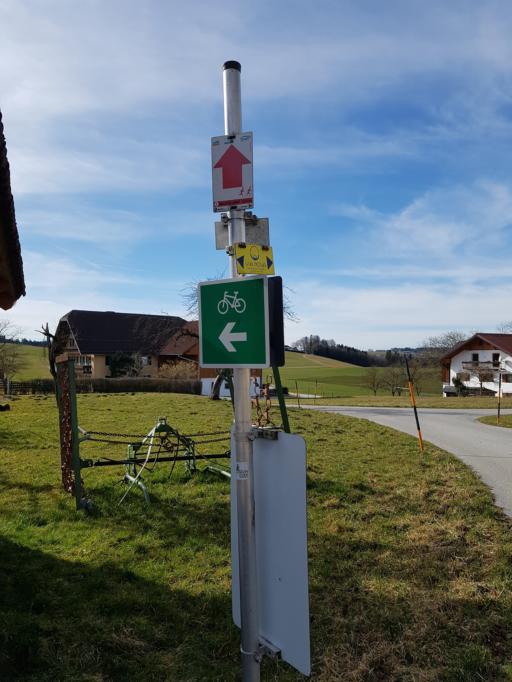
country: AT
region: Salzburg
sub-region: Politischer Bezirk Salzburg-Umgebung
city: Seekirchen am Wallersee
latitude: 47.8977
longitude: 13.1502
